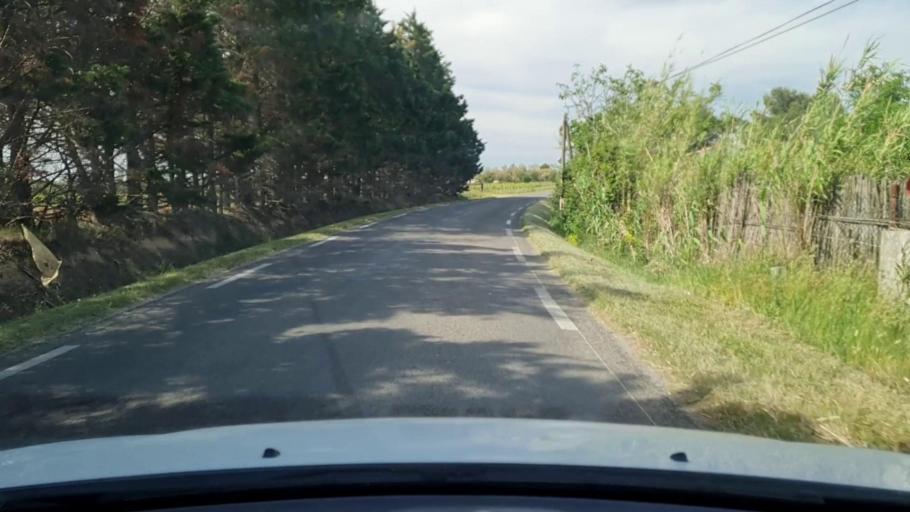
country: FR
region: Languedoc-Roussillon
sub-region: Departement du Gard
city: Aigues-Mortes
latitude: 43.6037
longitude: 4.2131
